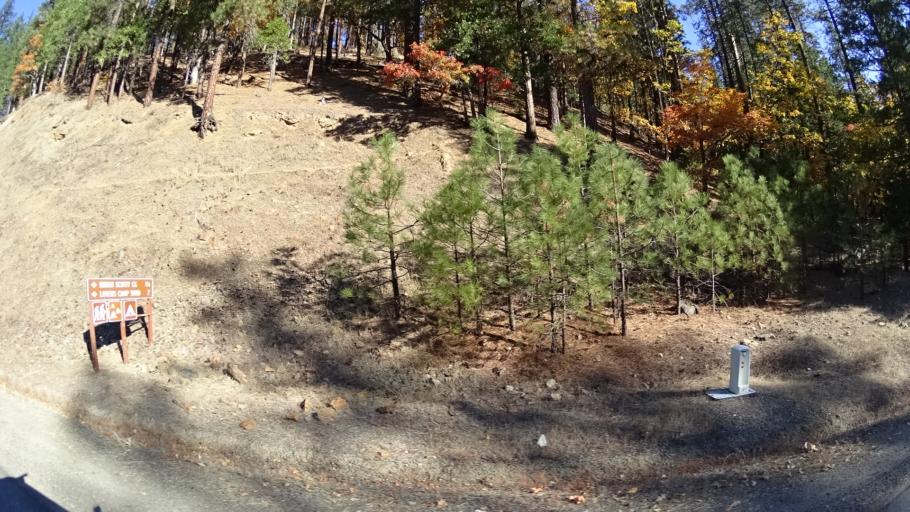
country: US
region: California
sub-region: Siskiyou County
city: Happy Camp
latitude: 41.6359
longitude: -123.0747
